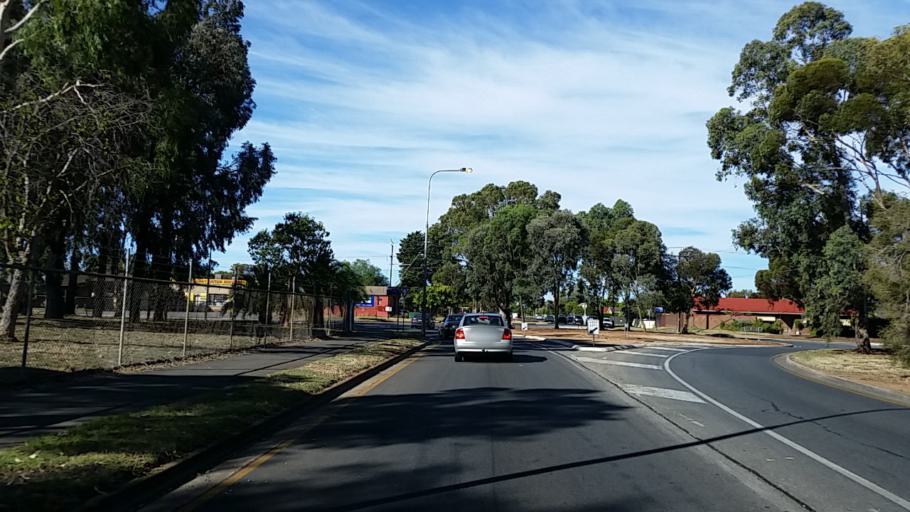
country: AU
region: South Australia
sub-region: Salisbury
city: Salisbury
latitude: -34.7775
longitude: 138.6436
